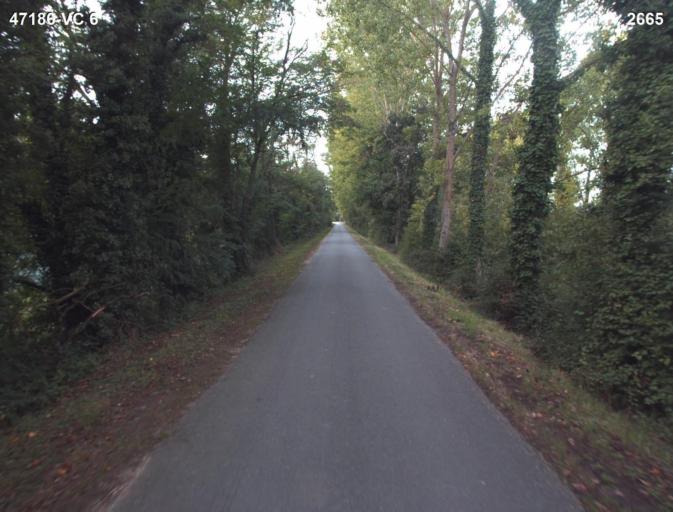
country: FR
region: Aquitaine
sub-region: Departement du Lot-et-Garonne
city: Sainte-Colombe-en-Bruilhois
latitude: 44.2175
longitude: 0.4644
